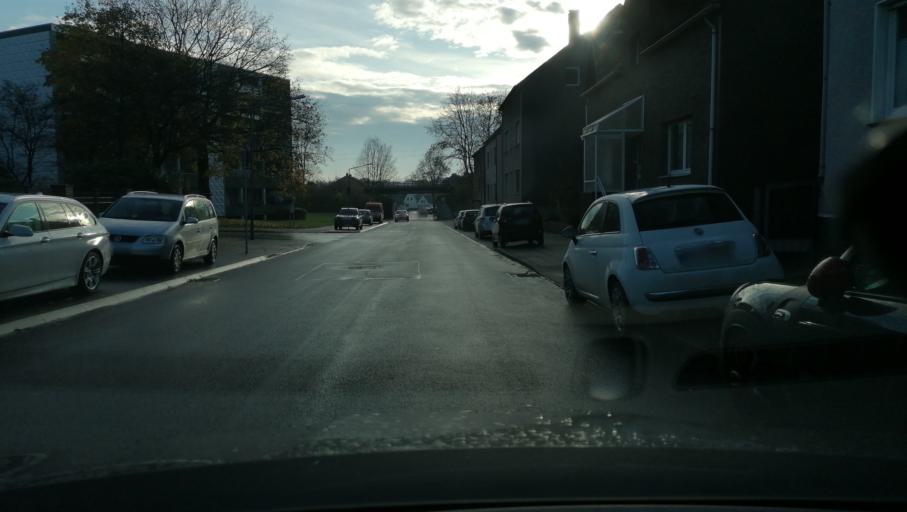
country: DE
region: North Rhine-Westphalia
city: Herten
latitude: 51.6004
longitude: 7.1545
